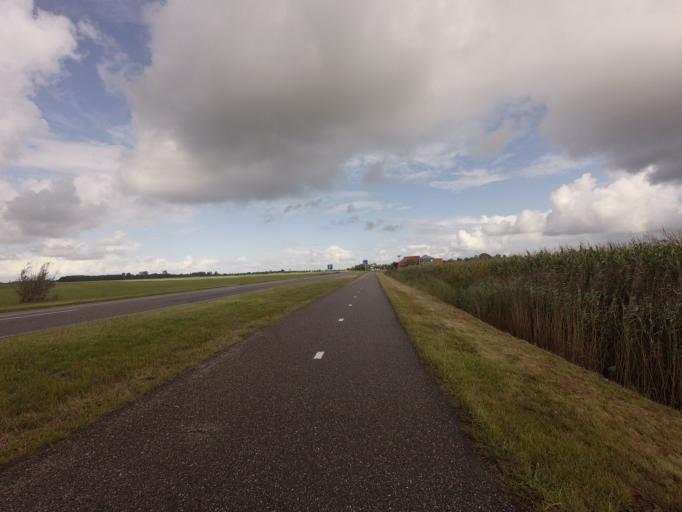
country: NL
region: Friesland
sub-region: Gemeente Tytsjerksteradiel
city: Garyp
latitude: 53.1549
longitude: 5.9516
